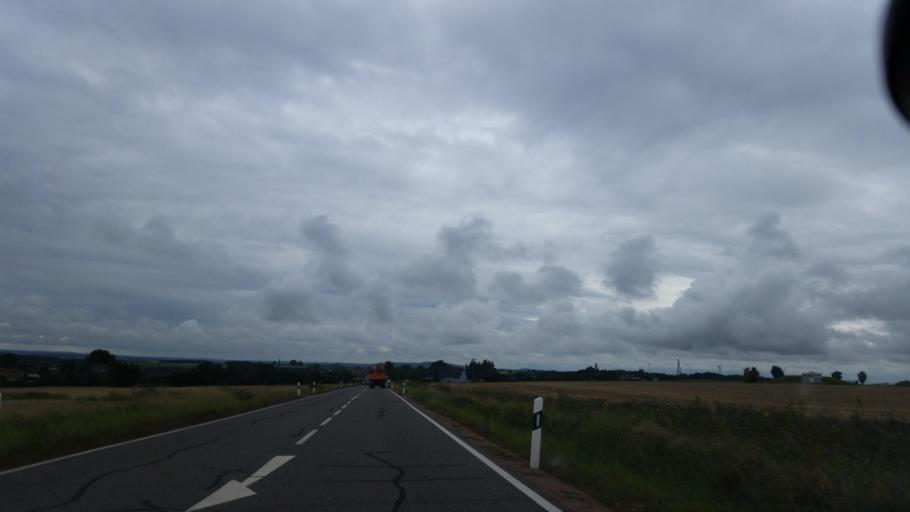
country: DE
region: Saxony
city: Geringswalde
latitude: 51.0894
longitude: 12.9263
